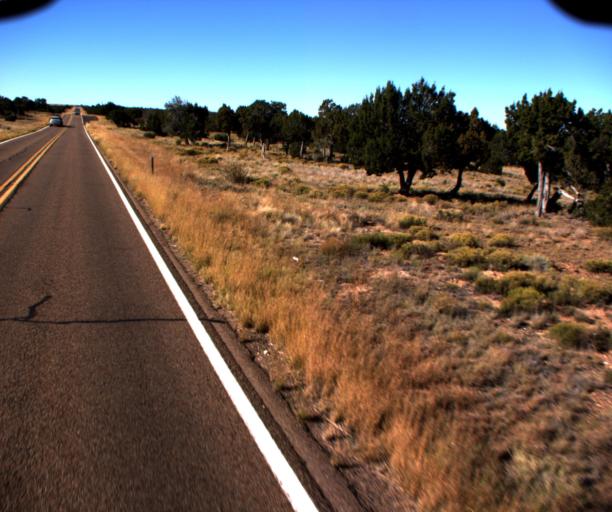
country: US
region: Arizona
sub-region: Navajo County
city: Heber-Overgaard
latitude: 34.4880
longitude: -110.4596
